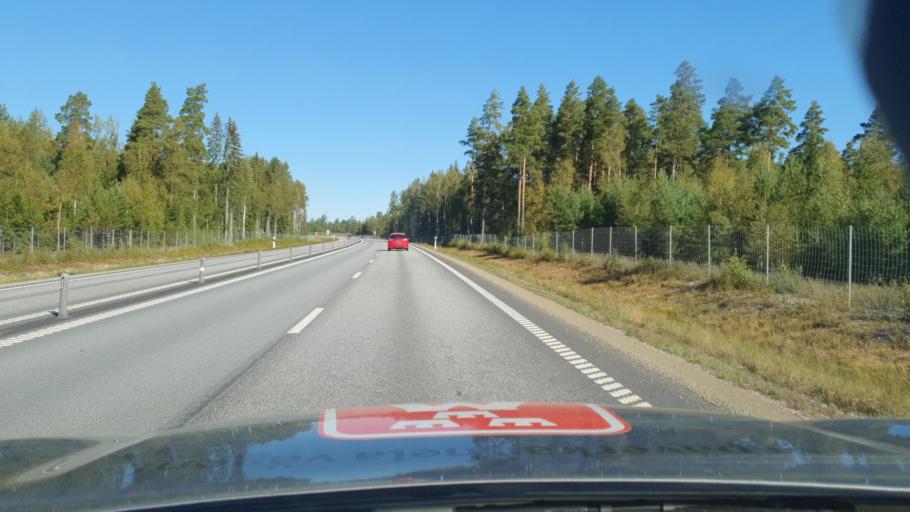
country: SE
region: OErebro
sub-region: Hallsbergs Kommun
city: Skollersta
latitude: 59.1052
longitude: 15.3078
